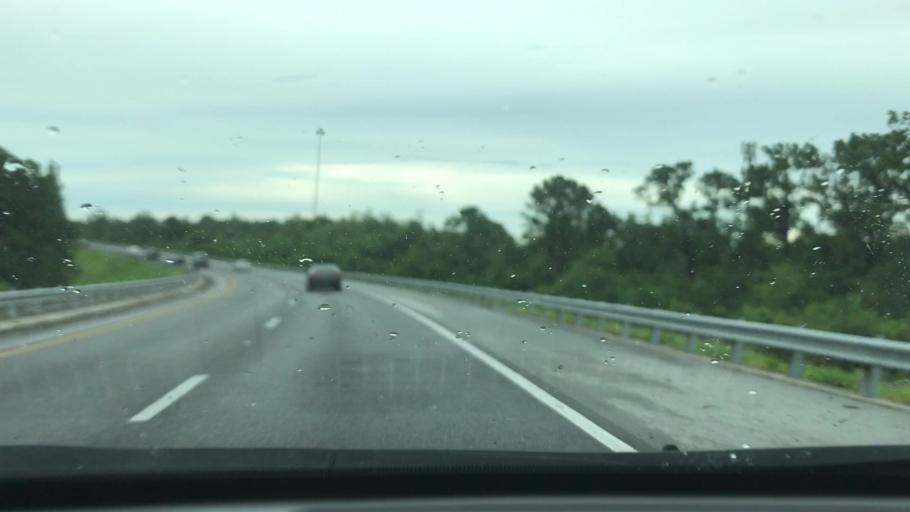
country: US
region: Florida
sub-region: Osceola County
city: Celebration
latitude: 28.3567
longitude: -81.5223
